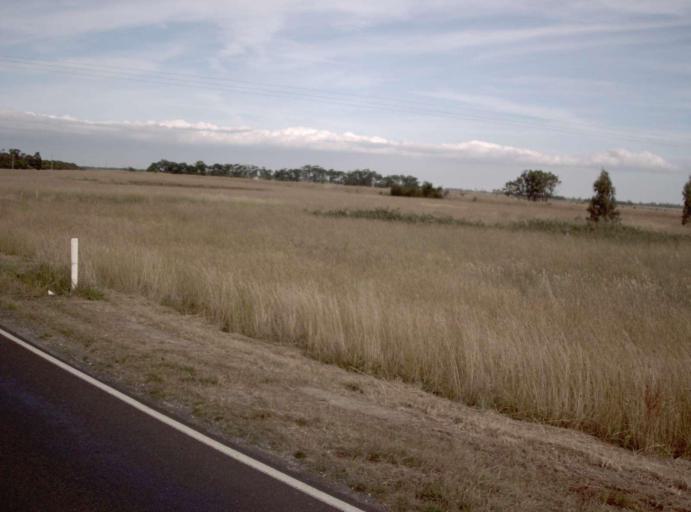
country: AU
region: Victoria
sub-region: Wellington
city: Heyfield
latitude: -38.0193
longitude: 146.7355
